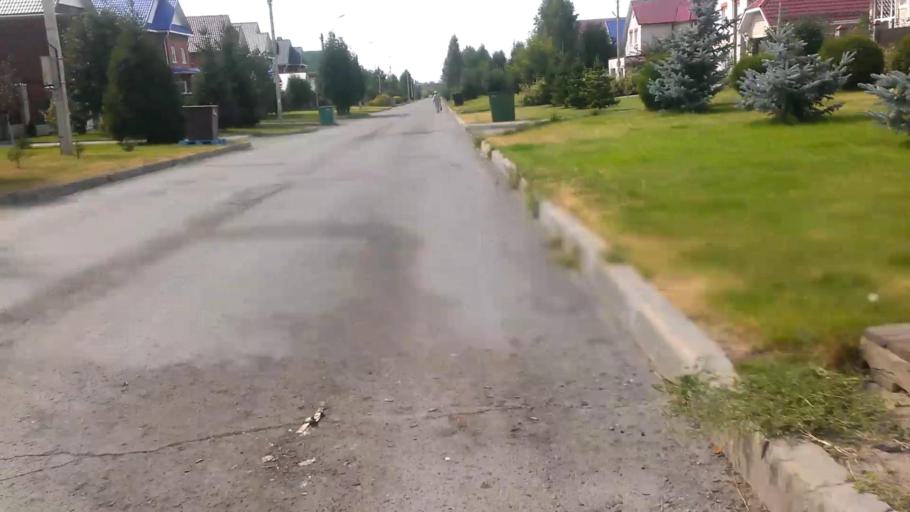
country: RU
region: Altai Krai
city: Novosilikatnyy
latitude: 53.3568
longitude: 83.6546
